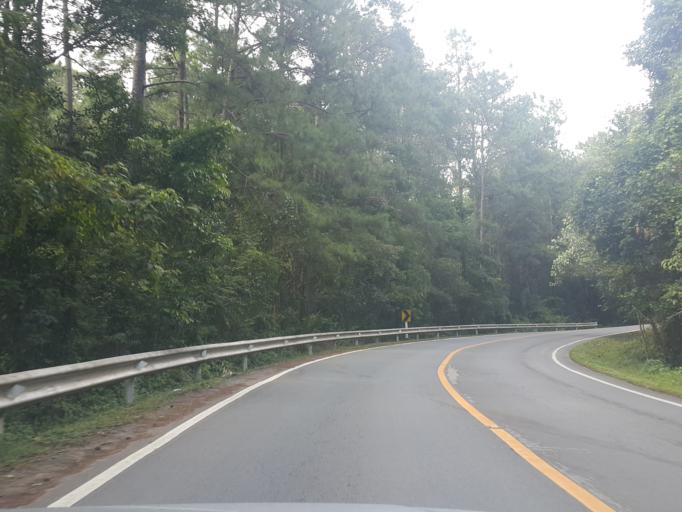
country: TH
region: Chiang Mai
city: Chom Thong
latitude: 18.5400
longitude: 98.5698
